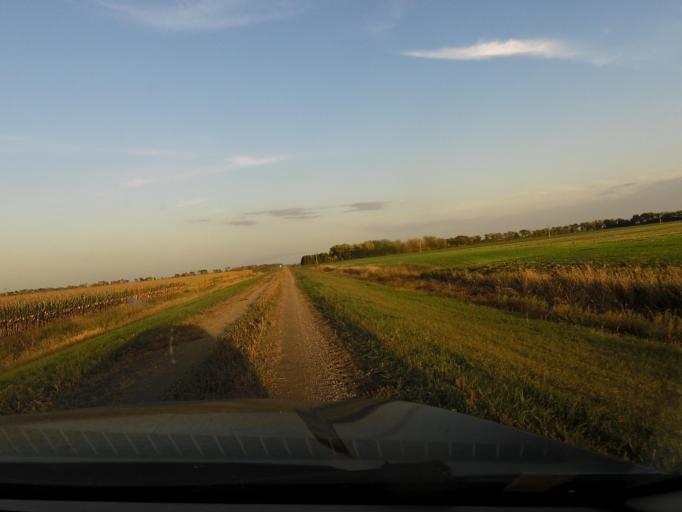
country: US
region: North Dakota
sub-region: Walsh County
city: Grafton
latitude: 48.3975
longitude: -97.2376
